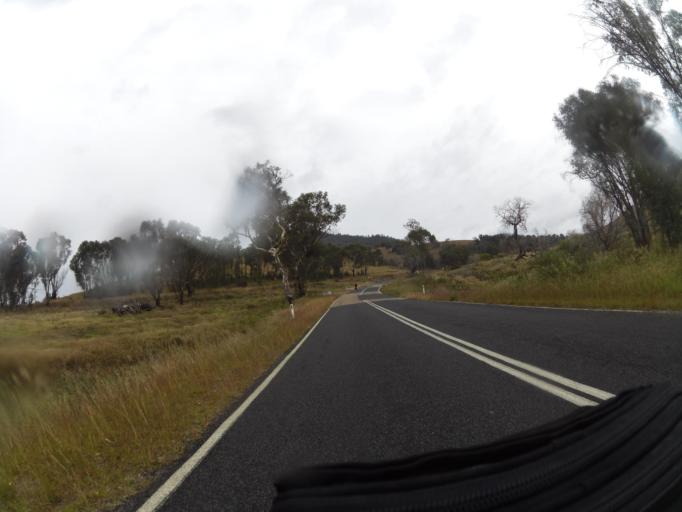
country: AU
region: New South Wales
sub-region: Greater Hume Shire
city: Holbrook
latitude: -36.2203
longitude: 147.7298
